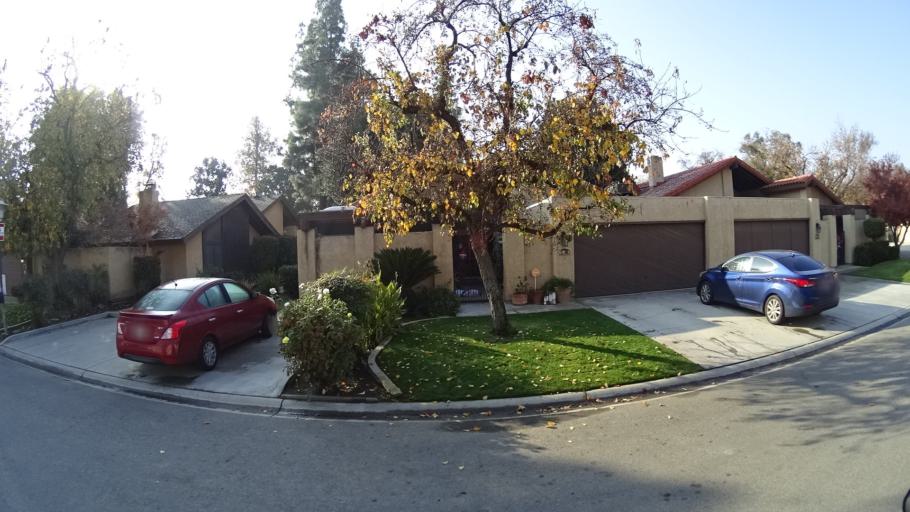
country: US
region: California
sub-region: Kern County
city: Greenacres
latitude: 35.3336
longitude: -119.0785
